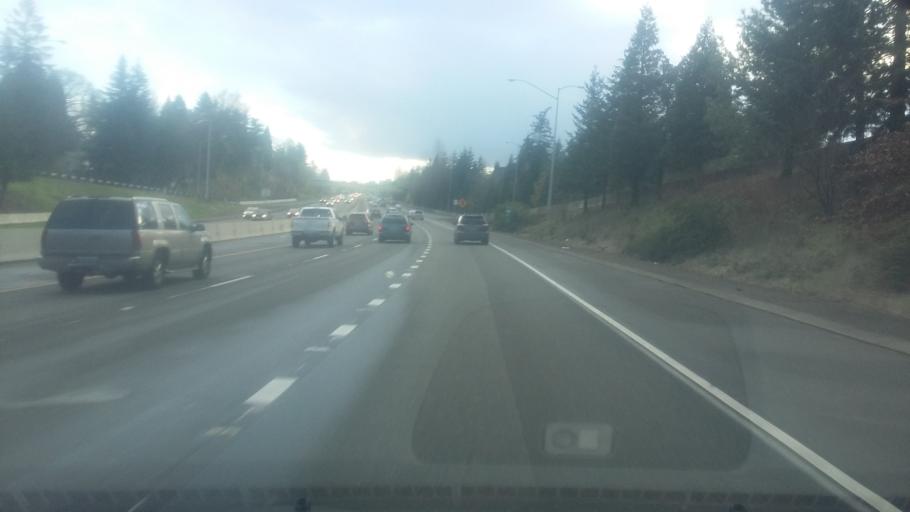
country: US
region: Oregon
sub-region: Washington County
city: Cedar Hills
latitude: 45.4985
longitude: -122.7909
